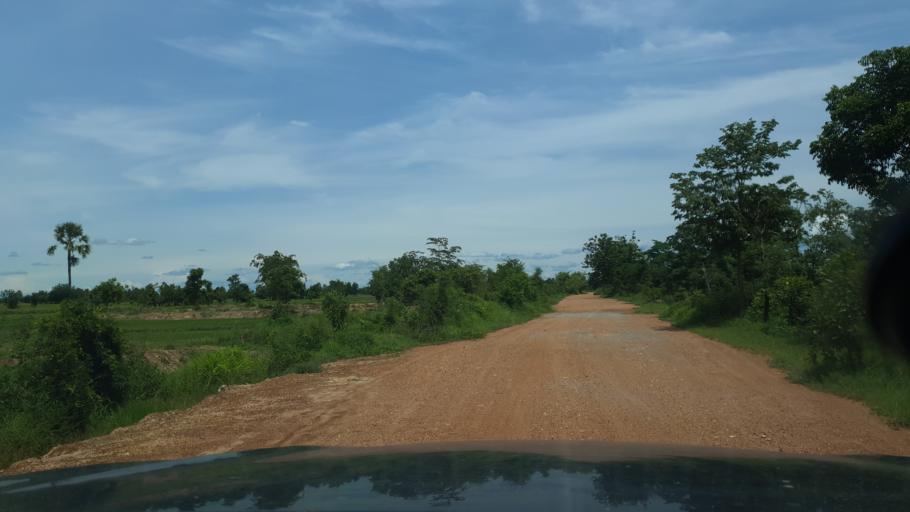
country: TH
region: Sukhothai
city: Ban Na
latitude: 17.0672
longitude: 99.7059
